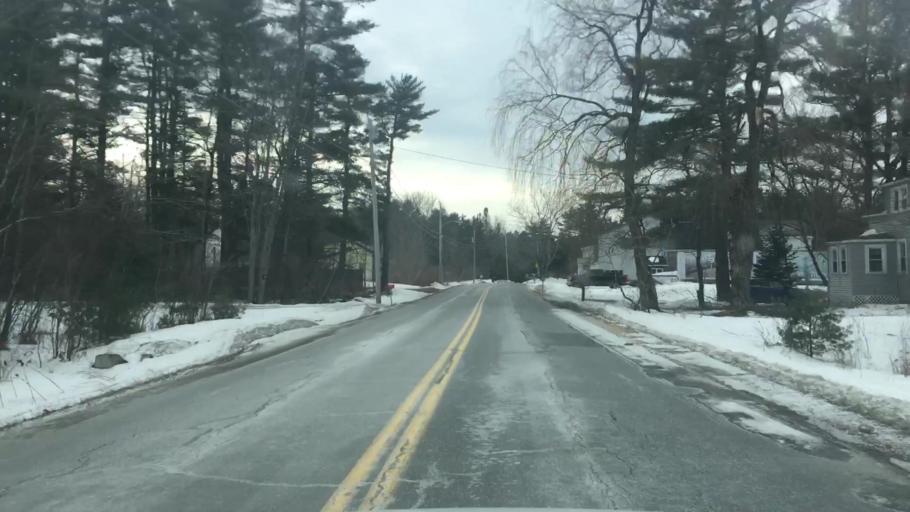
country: US
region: Maine
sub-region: Kennebec County
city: Chelsea
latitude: 44.2890
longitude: -69.6993
